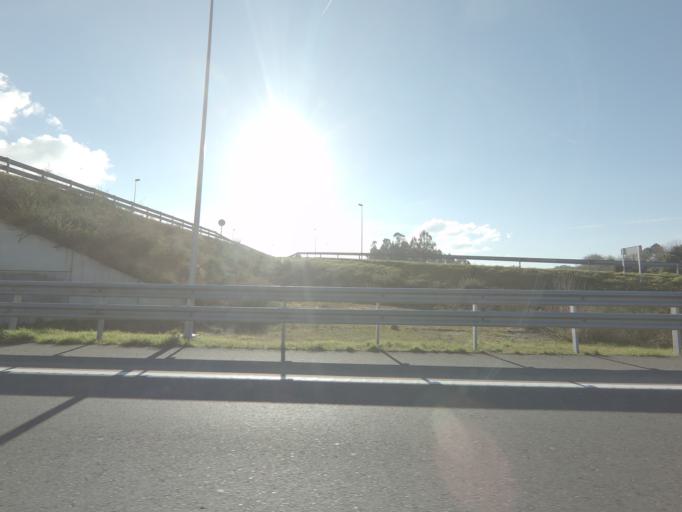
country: ES
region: Galicia
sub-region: Provincia de Pontevedra
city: Silleda
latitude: 42.7182
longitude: -8.2834
